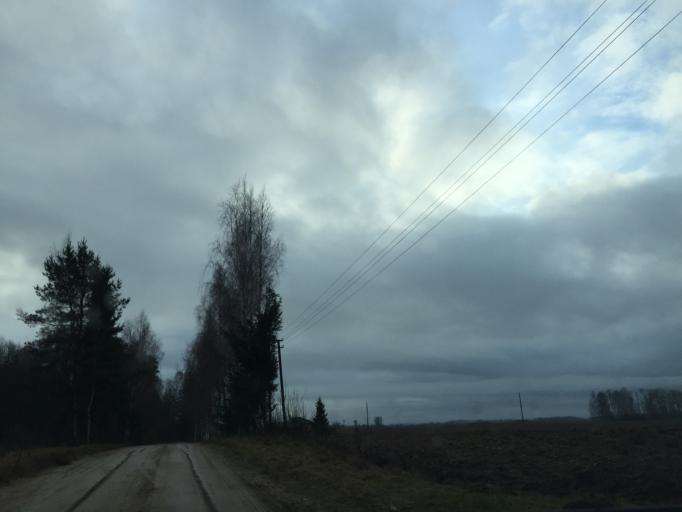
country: LV
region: Vainode
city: Vainode
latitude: 56.6073
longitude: 21.7989
